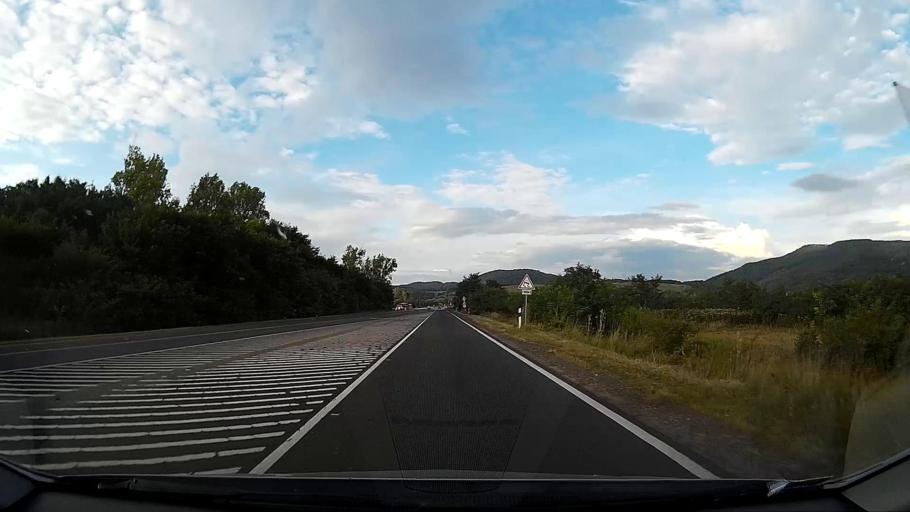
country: HU
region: Nograd
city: Tar
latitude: 47.9575
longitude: 19.7309
